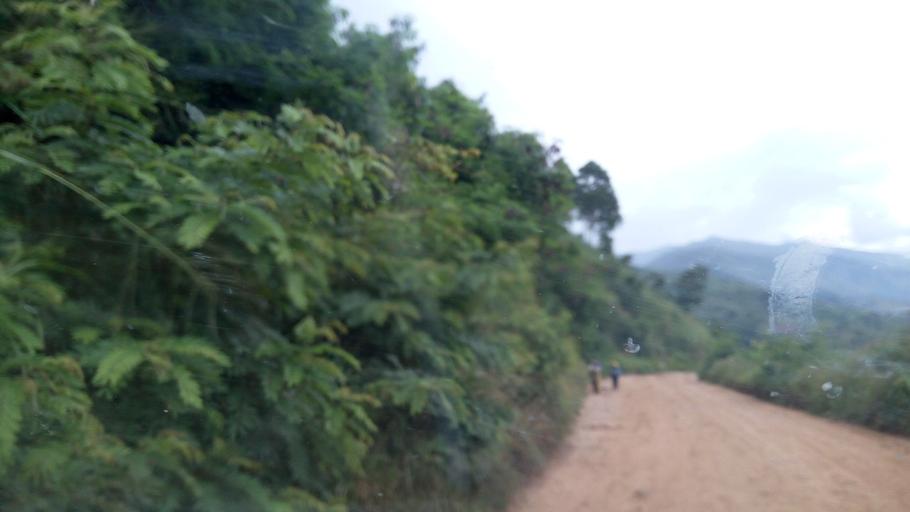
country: CD
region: South Kivu
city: Uvira
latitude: -3.5091
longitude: 29.1445
